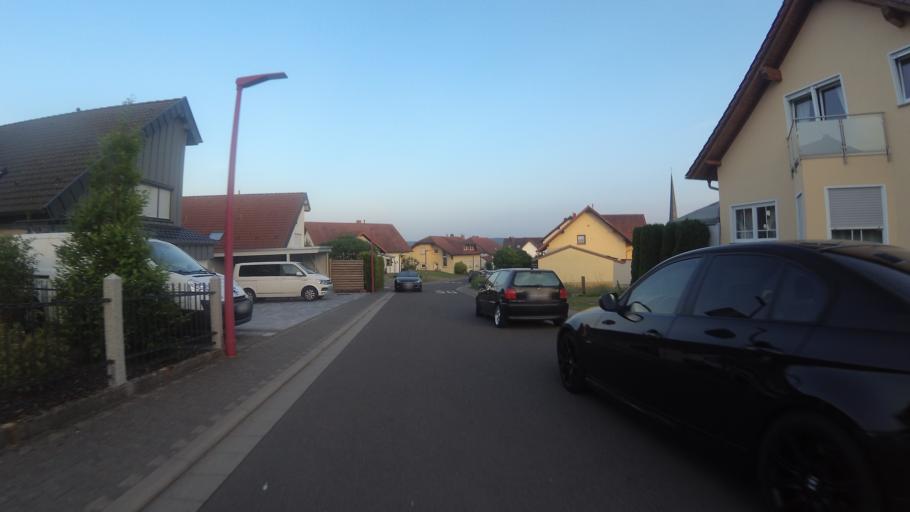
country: DE
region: Rheinland-Pfalz
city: Gries
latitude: 49.4210
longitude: 7.4031
